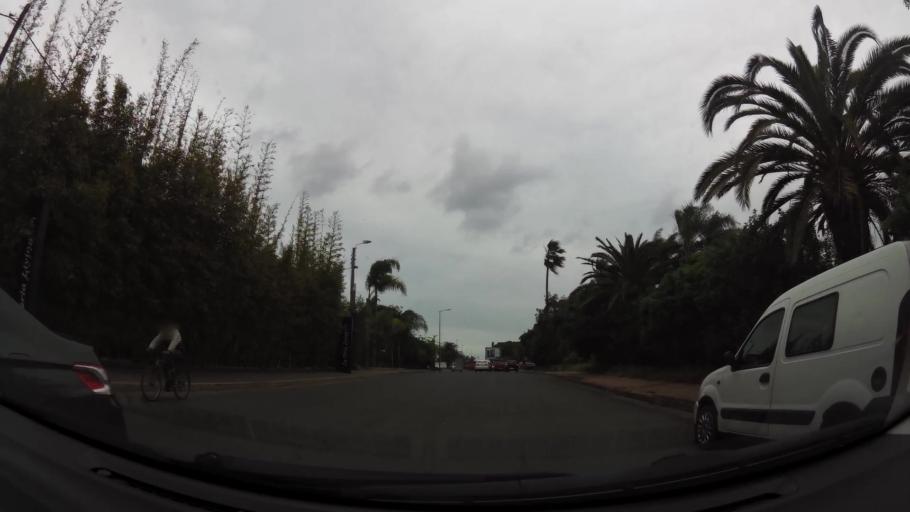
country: MA
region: Grand Casablanca
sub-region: Casablanca
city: Casablanca
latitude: 33.5897
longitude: -7.6539
